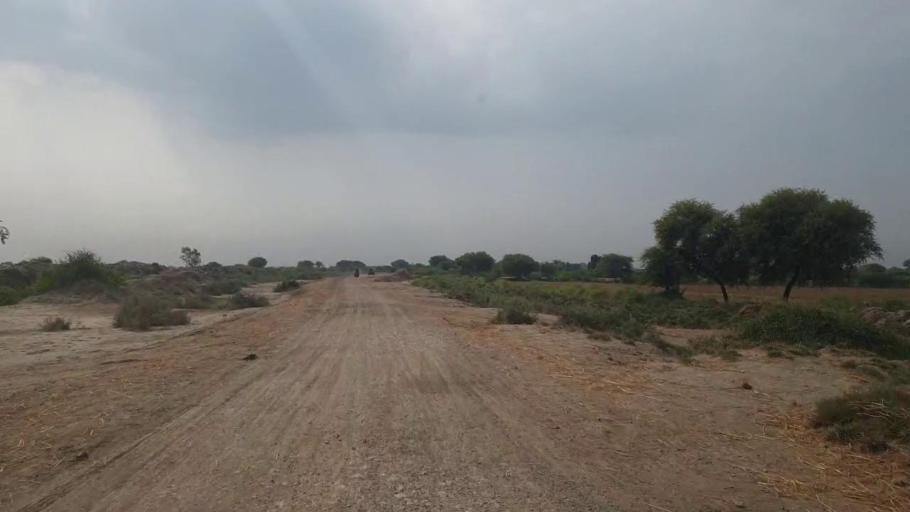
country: PK
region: Sindh
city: Talhar
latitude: 24.9268
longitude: 68.7861
